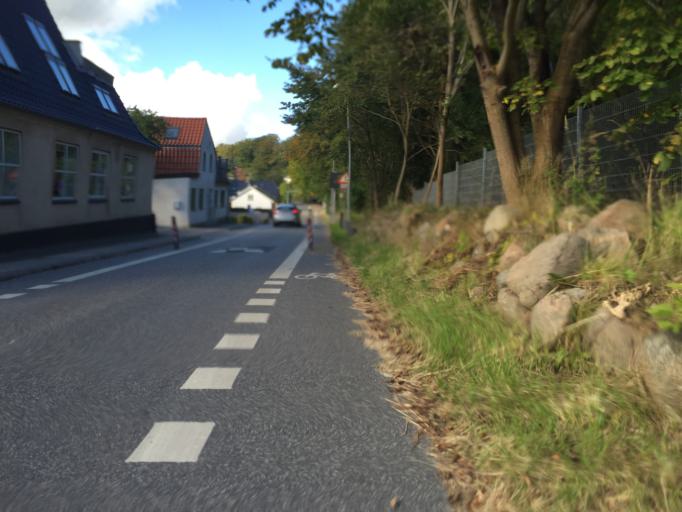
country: DK
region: Capital Region
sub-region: Fureso Kommune
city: Vaerlose
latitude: 55.7645
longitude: 12.4060
